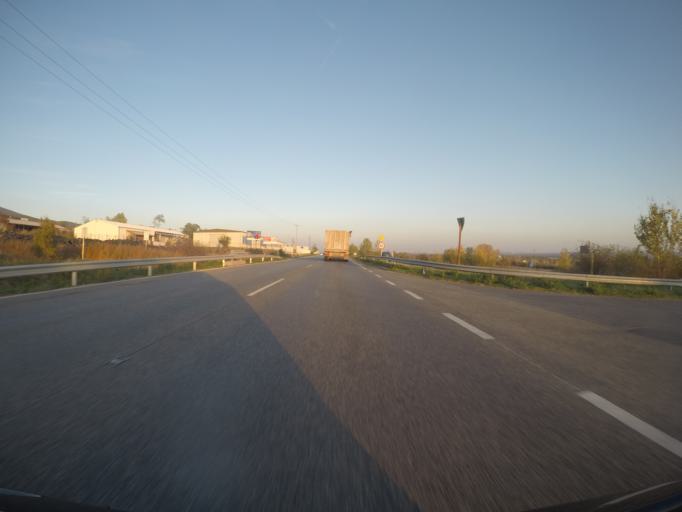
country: HU
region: Baranya
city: Pellerd
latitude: 46.0616
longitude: 18.1334
